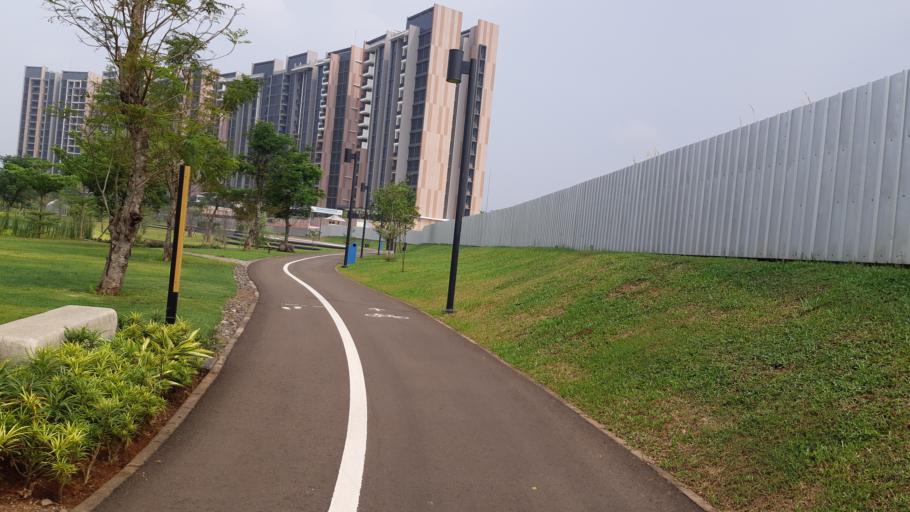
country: ID
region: West Java
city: Serpong
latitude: -6.2945
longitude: 106.6512
